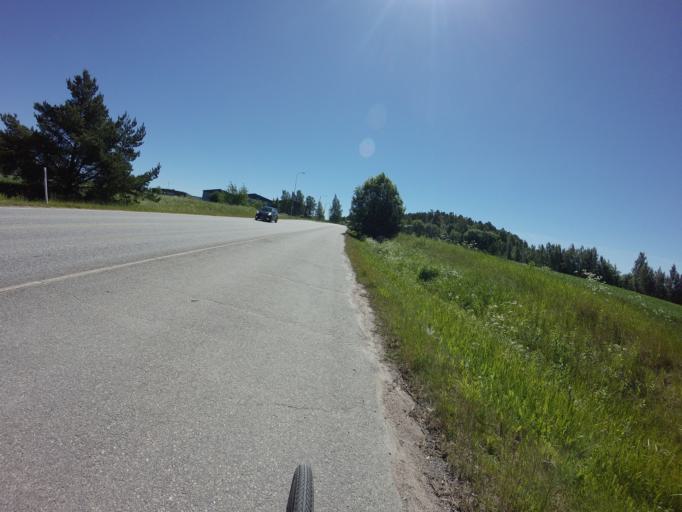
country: FI
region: Varsinais-Suomi
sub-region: Turku
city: Turku
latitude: 60.4947
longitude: 22.3338
